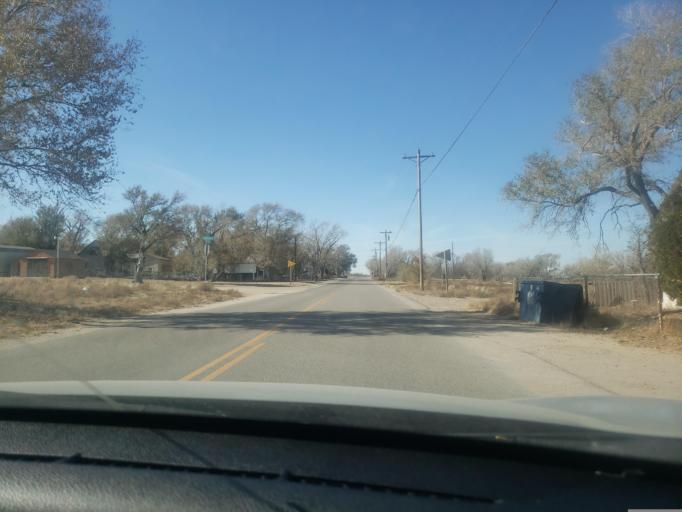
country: US
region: Kansas
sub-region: Finney County
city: Garden City
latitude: 37.9513
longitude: -100.8744
